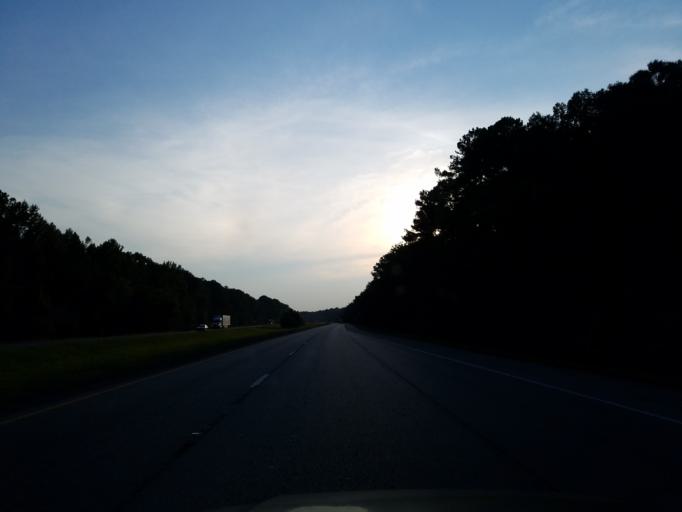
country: US
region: Mississippi
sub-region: Lauderdale County
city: Marion
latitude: 32.4136
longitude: -88.5104
